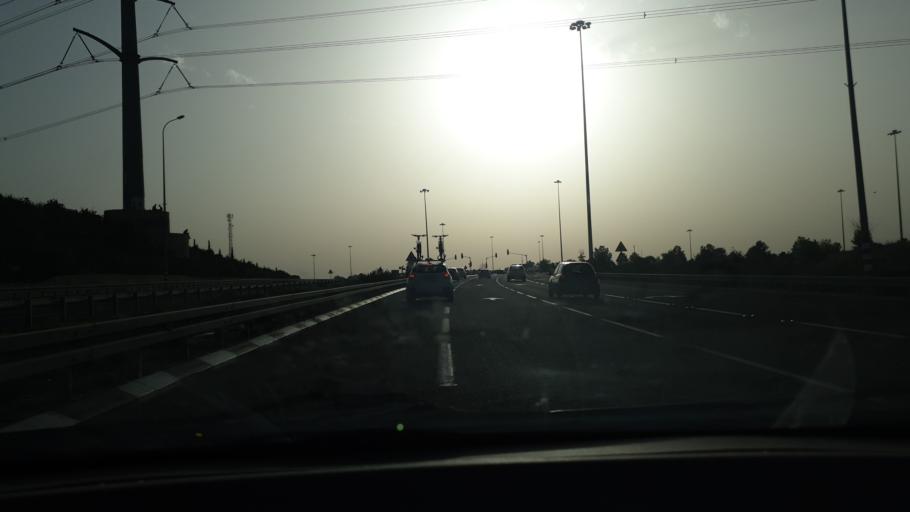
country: IL
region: Central District
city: Even Yehuda
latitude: 32.2560
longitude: 34.8958
